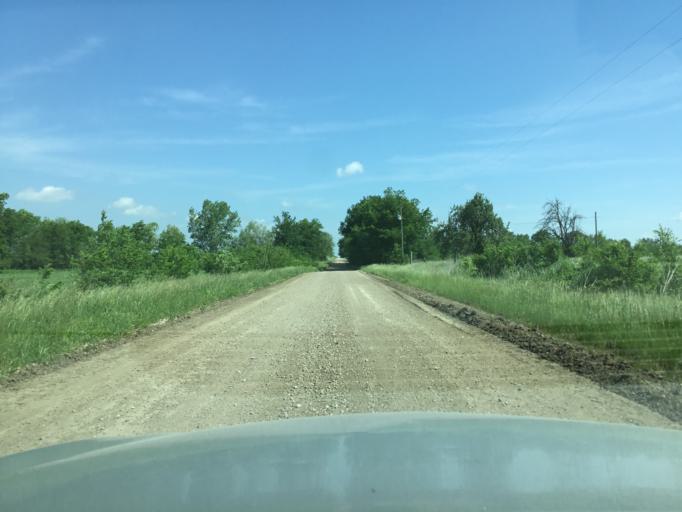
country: US
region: Kansas
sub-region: Labette County
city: Oswego
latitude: 37.1837
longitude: -95.1399
